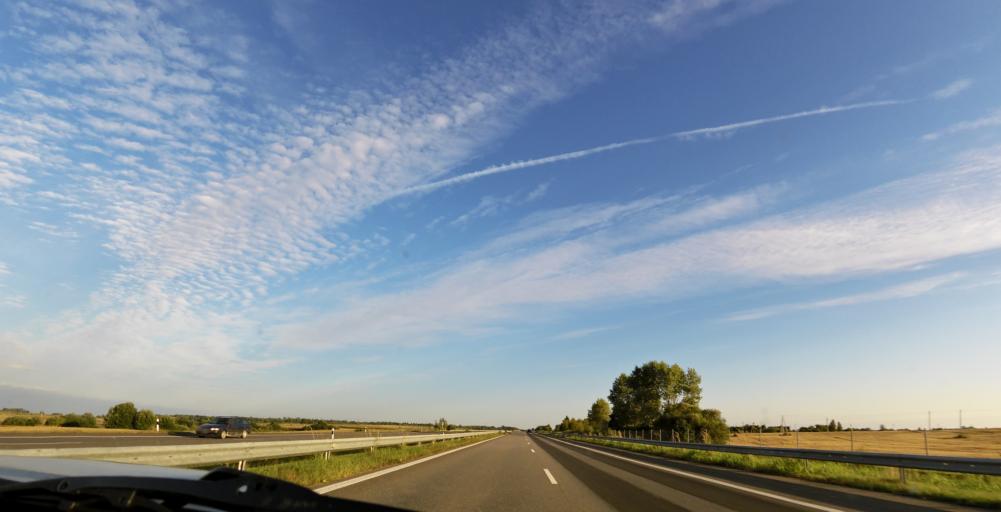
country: LT
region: Vilnius County
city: Ukmerge
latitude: 55.1549
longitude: 24.8220
